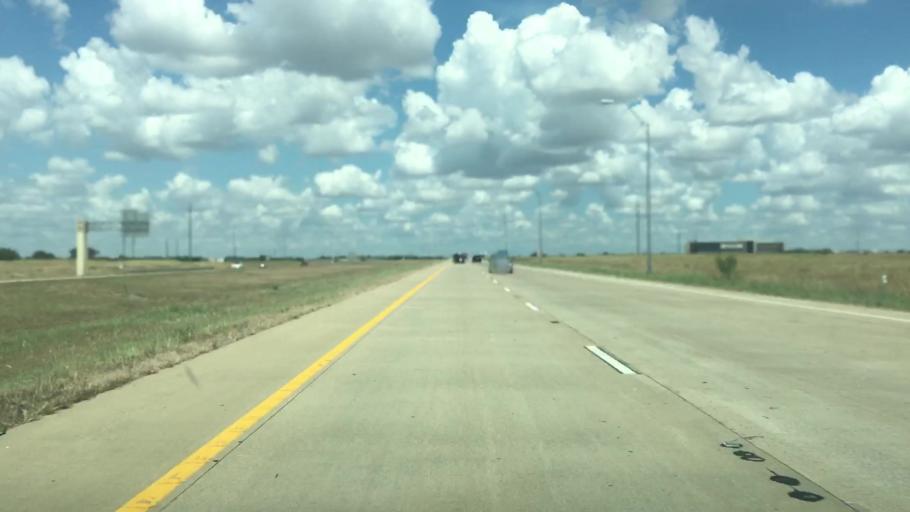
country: US
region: Texas
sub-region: Williamson County
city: Hutto
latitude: 30.5458
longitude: -97.5764
